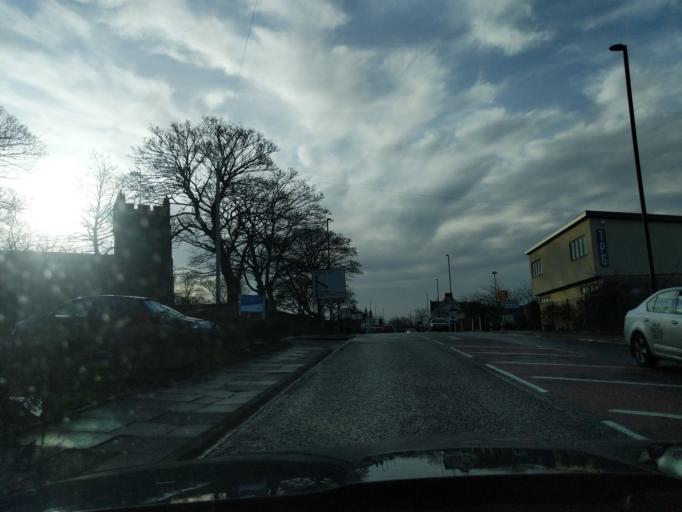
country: GB
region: England
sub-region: Borough of North Tyneside
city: Wallsend
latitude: 54.9947
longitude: -1.5175
